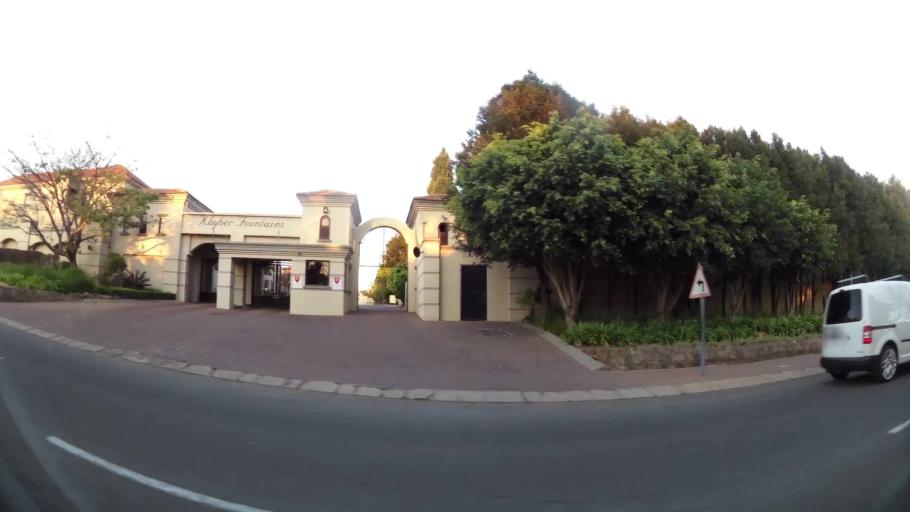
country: ZA
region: Gauteng
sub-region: City of Johannesburg Metropolitan Municipality
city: Midrand
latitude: -26.0549
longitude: 28.0859
